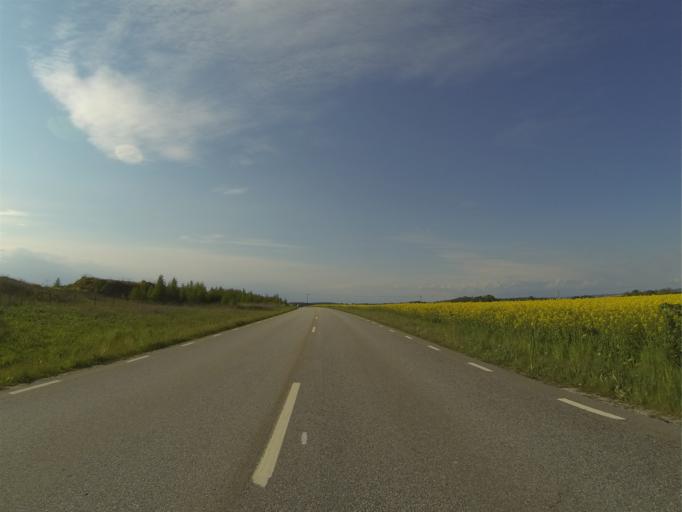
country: SE
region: Skane
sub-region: Lunds Kommun
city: Lund
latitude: 55.7038
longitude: 13.3035
